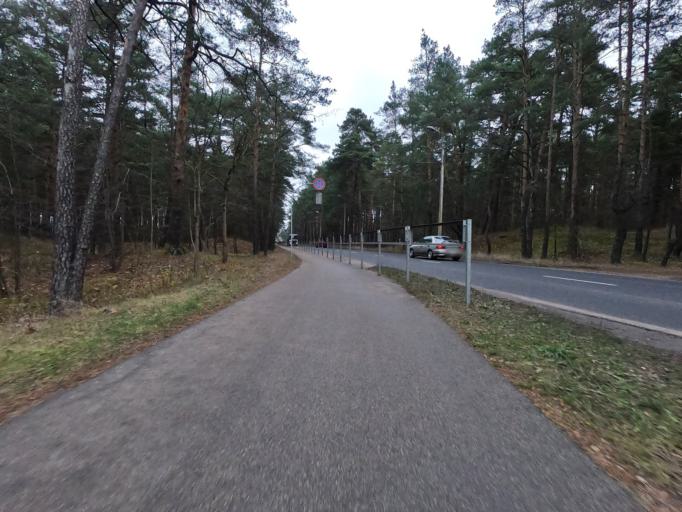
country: LV
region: Riga
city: Bolderaja
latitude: 57.0447
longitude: 24.1022
